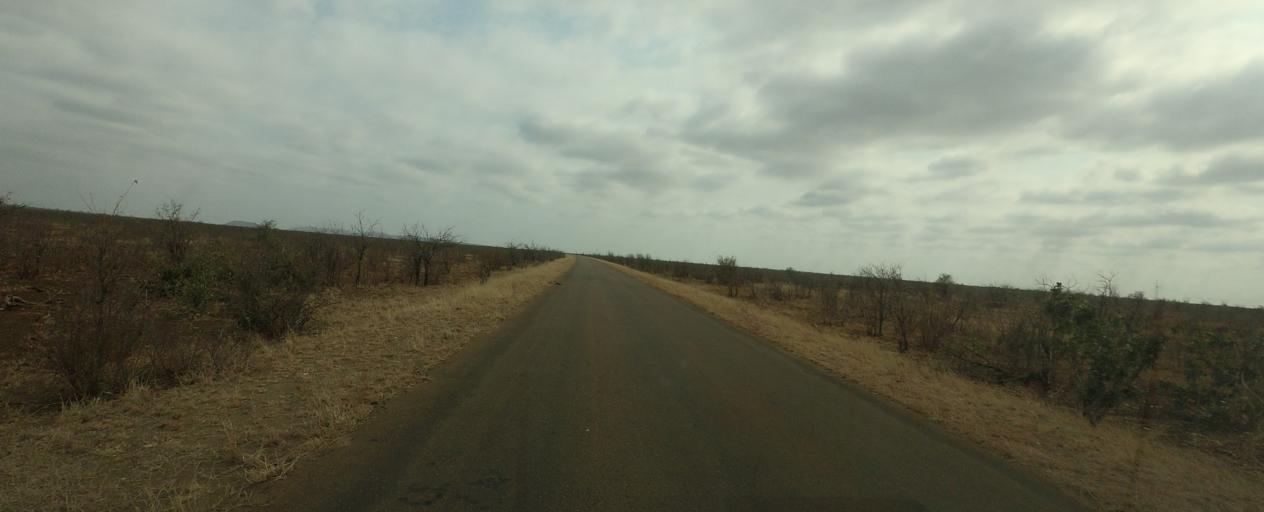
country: ZA
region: Limpopo
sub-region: Vhembe District Municipality
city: Mutale
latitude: -22.6795
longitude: 31.1671
